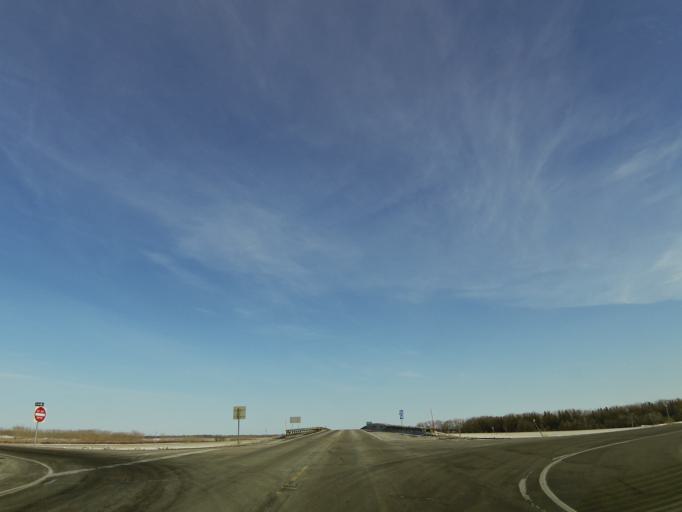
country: US
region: North Dakota
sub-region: Walsh County
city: Grafton
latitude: 48.4121
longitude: -97.1927
